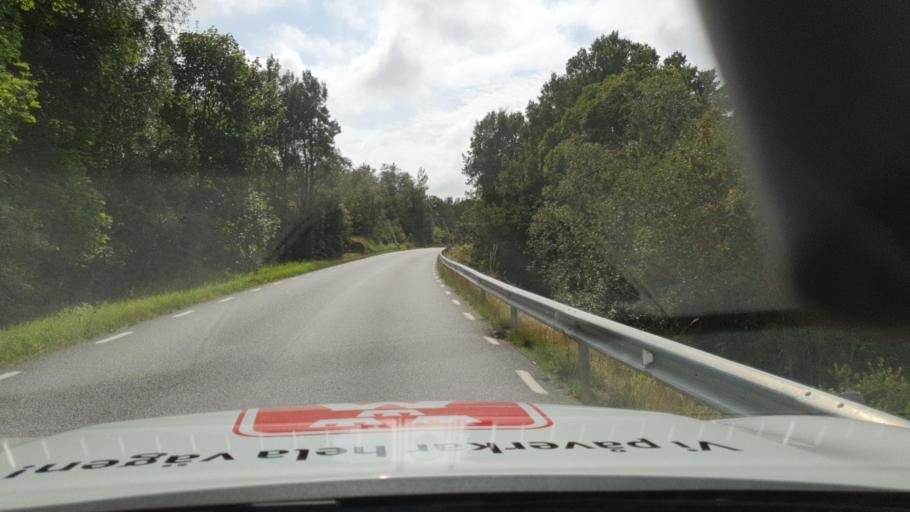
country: SE
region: Vaestra Goetaland
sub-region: Sotenas Kommun
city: Hunnebostrand
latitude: 58.5656
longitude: 11.2966
